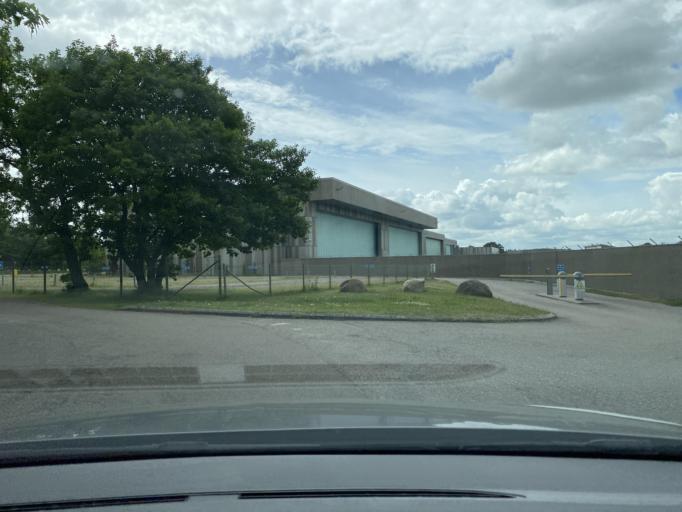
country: DK
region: South Denmark
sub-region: Billund Kommune
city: Billund
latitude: 55.7370
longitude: 9.1296
